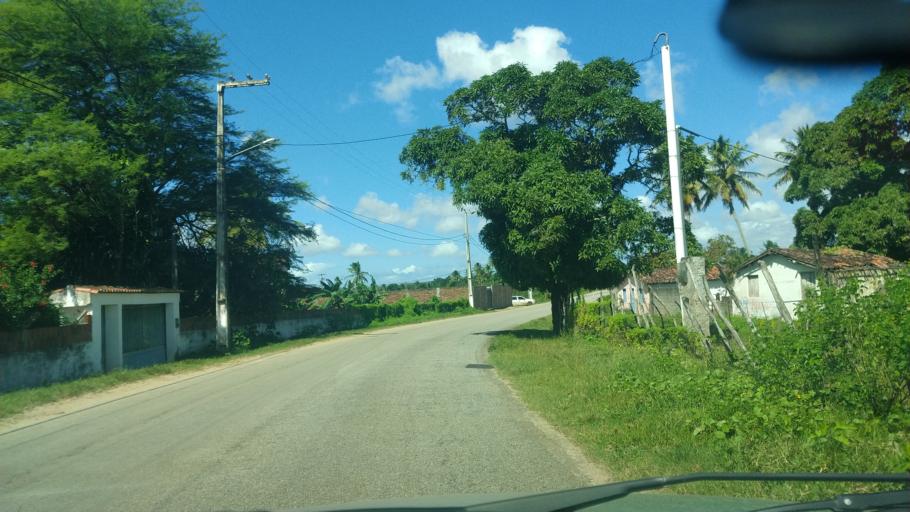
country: BR
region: Rio Grande do Norte
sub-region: Sao Goncalo Do Amarante
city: Sao Goncalo do Amarante
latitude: -5.8175
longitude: -35.3177
